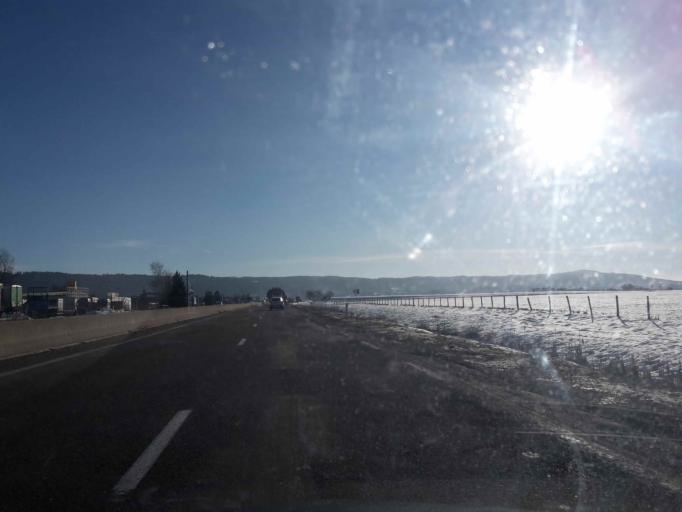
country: FR
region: Franche-Comte
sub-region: Departement du Doubs
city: Doubs
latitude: 46.9157
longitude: 6.3344
